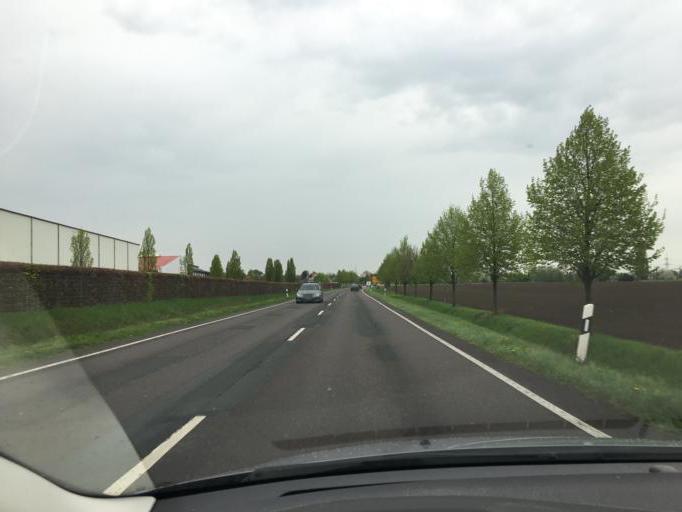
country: DE
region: Saxony-Anhalt
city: Gross Ammensleben
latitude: 52.2274
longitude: 11.5321
